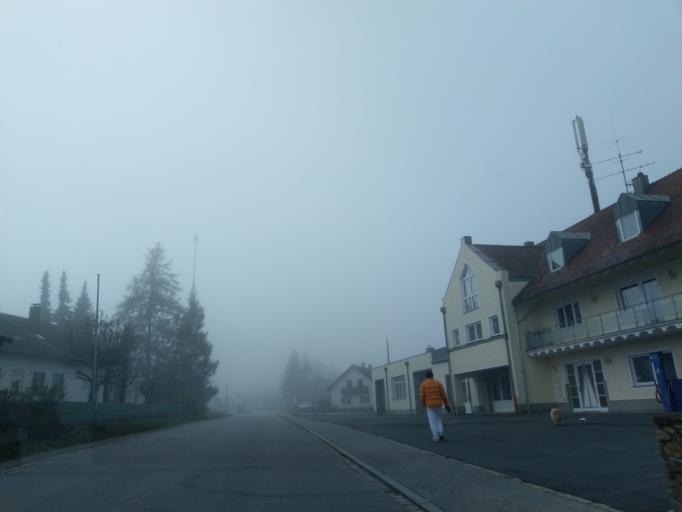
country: DE
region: Bavaria
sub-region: Lower Bavaria
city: Schollnach
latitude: 48.7528
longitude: 13.1729
